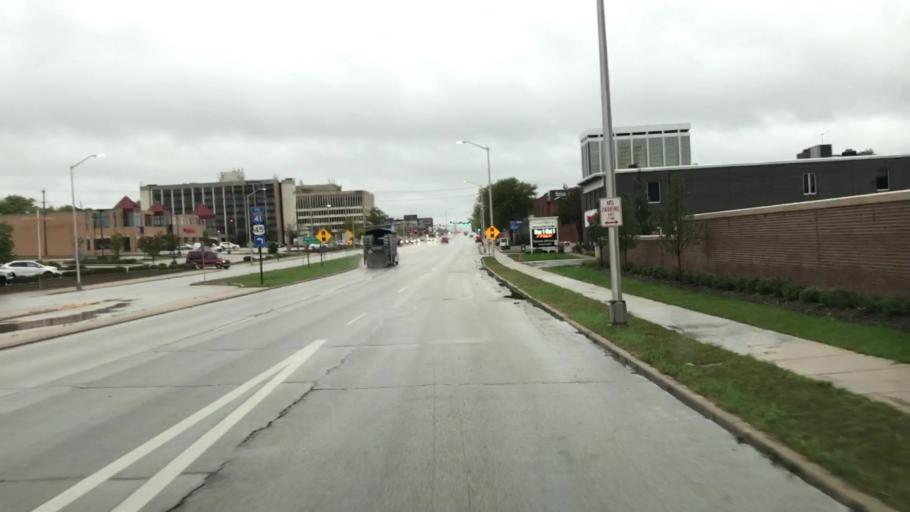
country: US
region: Wisconsin
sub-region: Waukesha County
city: Elm Grove
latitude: 43.0573
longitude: -88.0474
